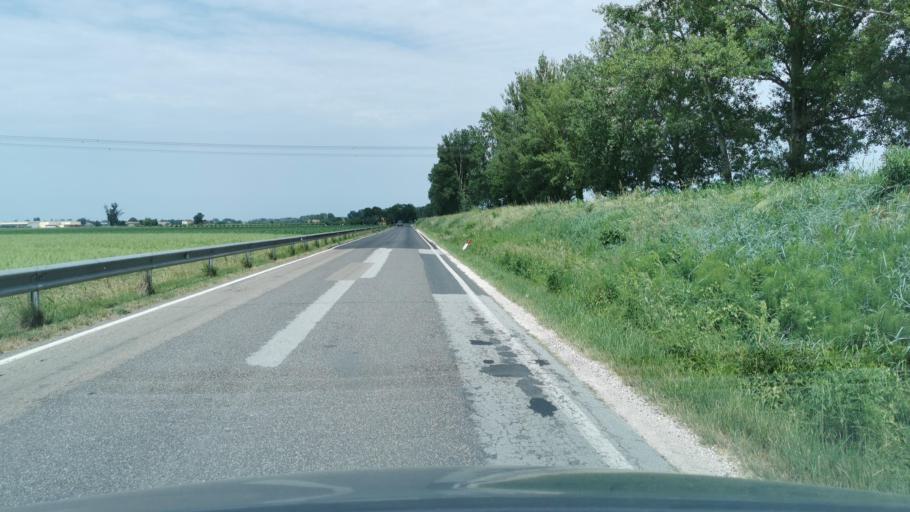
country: IT
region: Emilia-Romagna
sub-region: Provincia di Ravenna
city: Alfonsine
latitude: 44.4802
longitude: 12.0396
